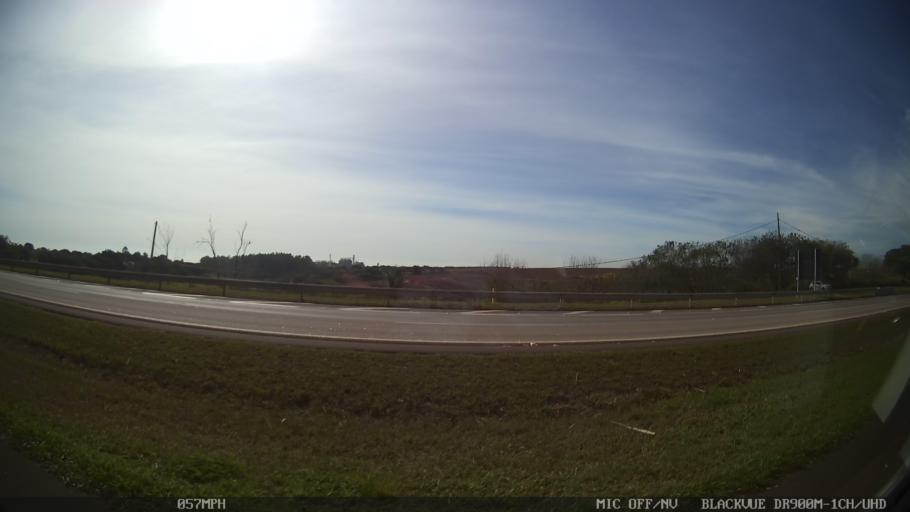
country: BR
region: Sao Paulo
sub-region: Rio Das Pedras
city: Rio das Pedras
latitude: -22.7779
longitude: -47.5899
